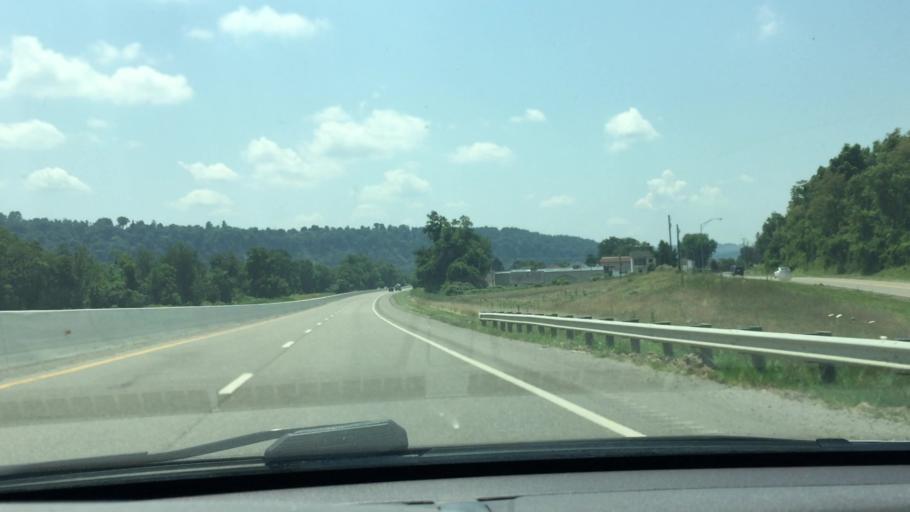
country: US
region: West Virginia
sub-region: Marshall County
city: McMechen
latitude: 39.9815
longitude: -80.7402
